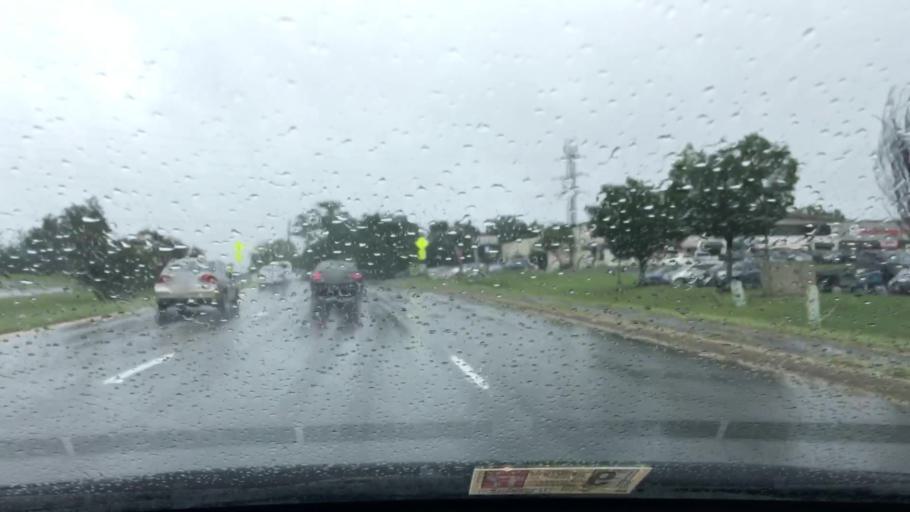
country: US
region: Virginia
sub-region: Loudoun County
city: Sterling
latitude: 38.9924
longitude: -77.4197
